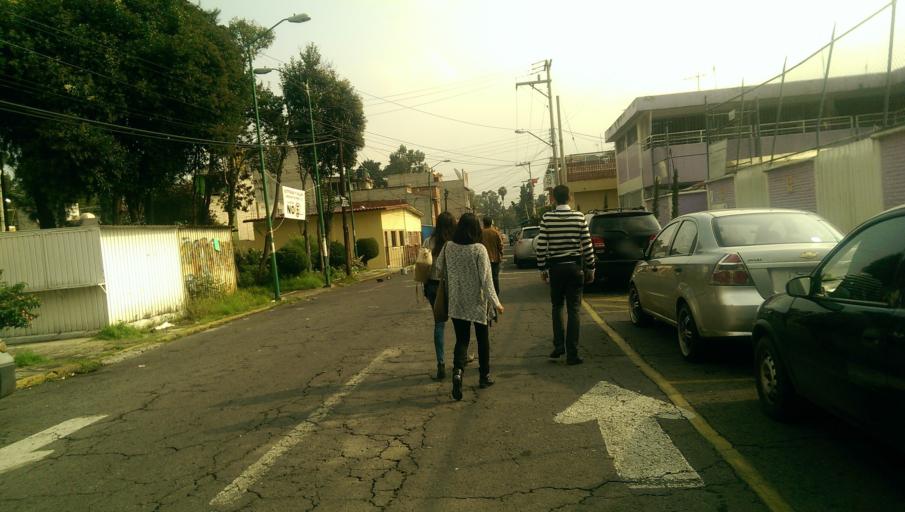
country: MX
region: Mexico City
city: Tlalpan
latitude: 19.2839
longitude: -99.1401
